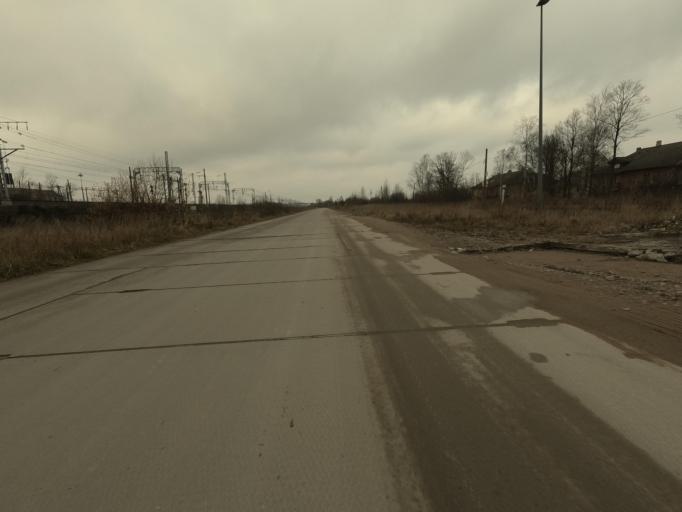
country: RU
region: Leningrad
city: Lyuban'
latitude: 59.4754
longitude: 31.2563
